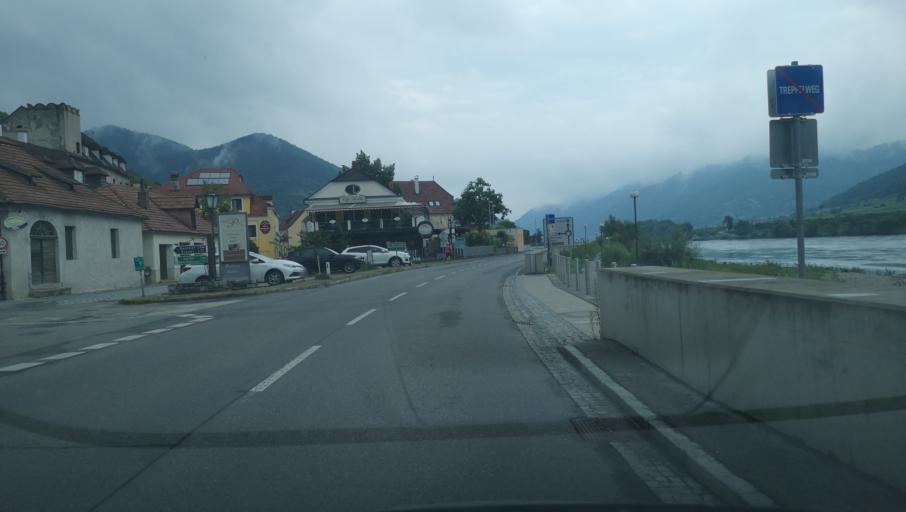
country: AT
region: Lower Austria
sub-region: Politischer Bezirk Krems
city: Spitz
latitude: 48.3581
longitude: 15.4096
